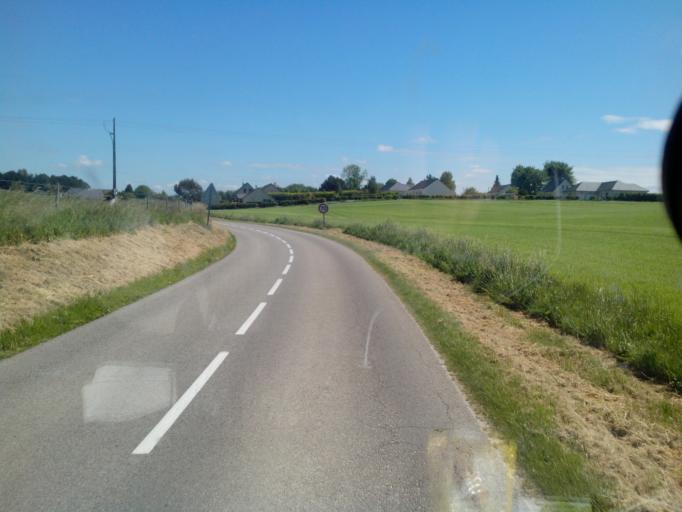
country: FR
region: Haute-Normandie
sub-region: Departement de la Seine-Maritime
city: Gonneville-la-Mallet
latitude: 49.6655
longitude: 0.1973
